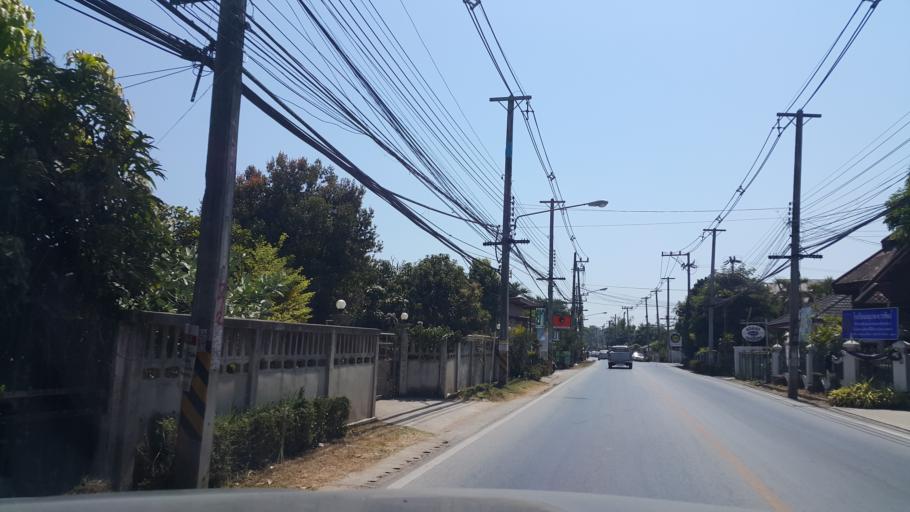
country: TH
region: Chiang Mai
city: San Sai
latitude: 18.8480
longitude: 99.0439
